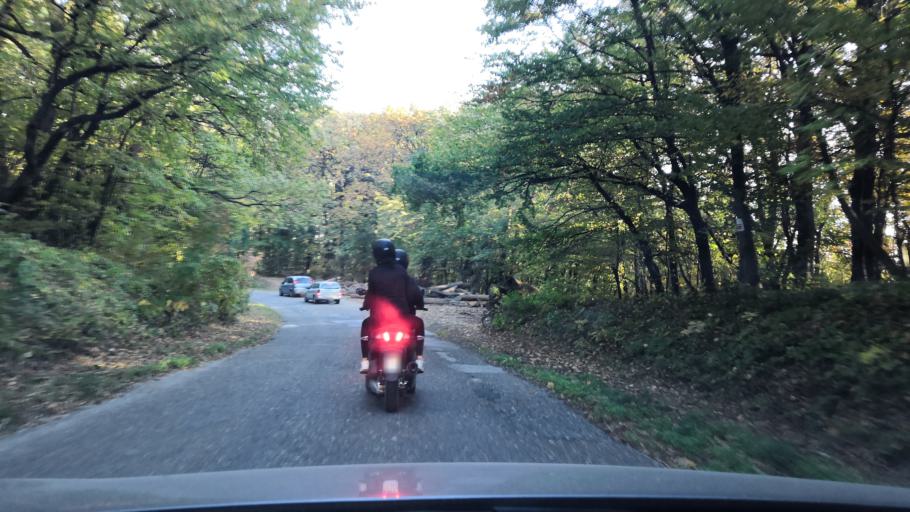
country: RS
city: Vrdnik
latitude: 45.1551
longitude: 19.8104
